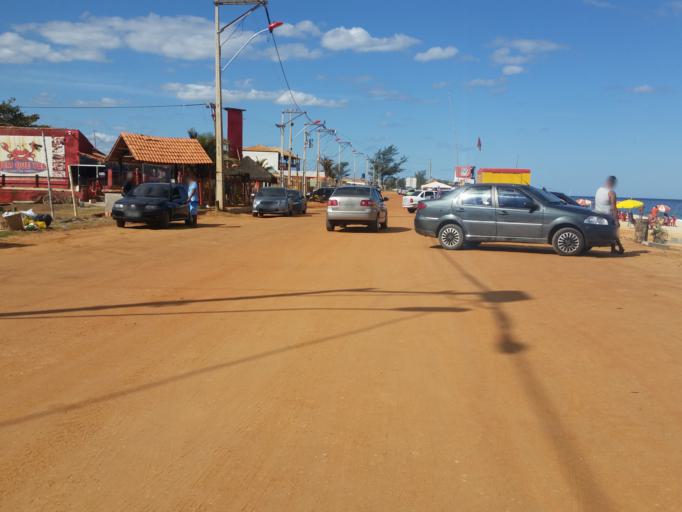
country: BR
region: Rio de Janeiro
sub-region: Marica
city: Marica
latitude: -22.9698
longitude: -42.9628
